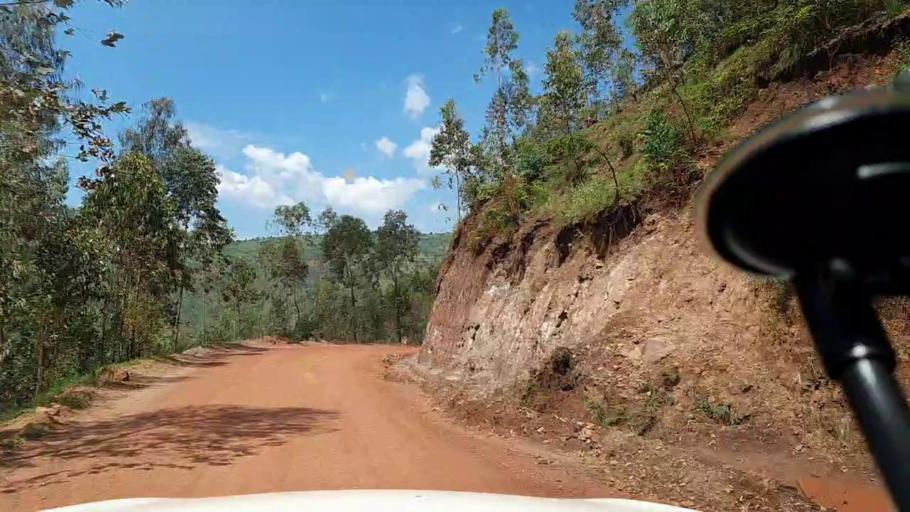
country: RW
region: Kigali
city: Kigali
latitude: -1.8002
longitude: 29.8905
